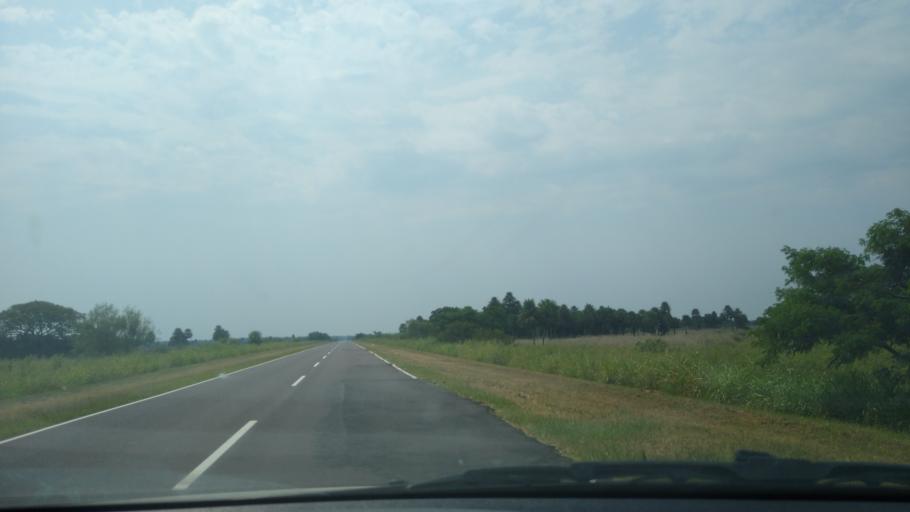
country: AR
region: Chaco
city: La Eduvigis
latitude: -26.9966
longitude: -58.9734
